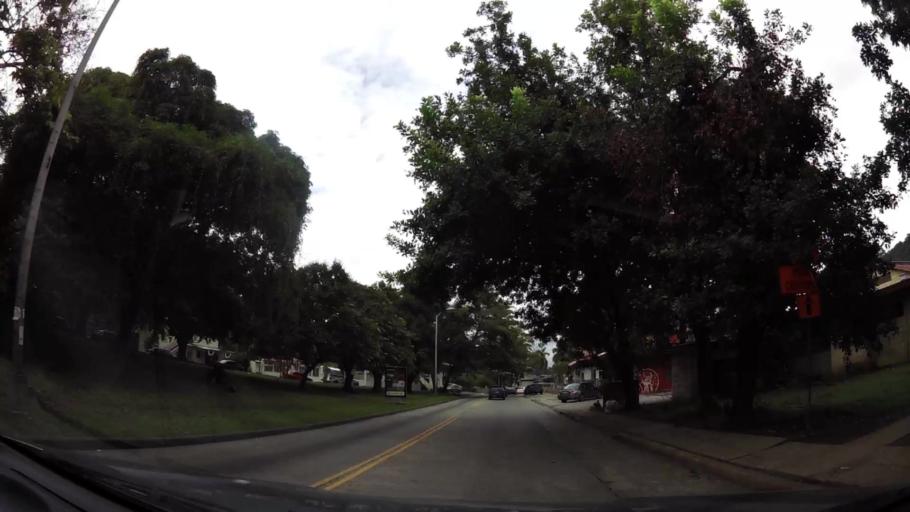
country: PA
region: Panama
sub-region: Distrito de Panama
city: Ancon
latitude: 8.9506
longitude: -79.5563
